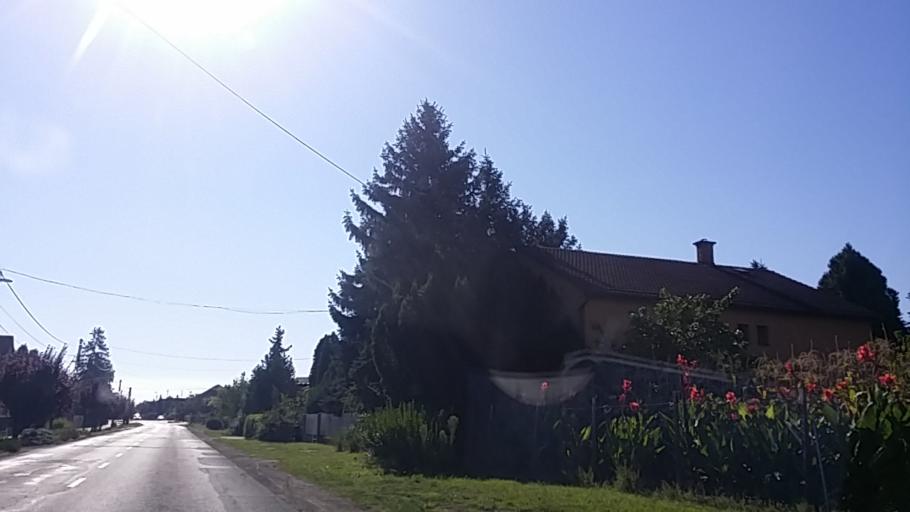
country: HU
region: Fejer
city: Racalmas
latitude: 47.0281
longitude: 18.9185
